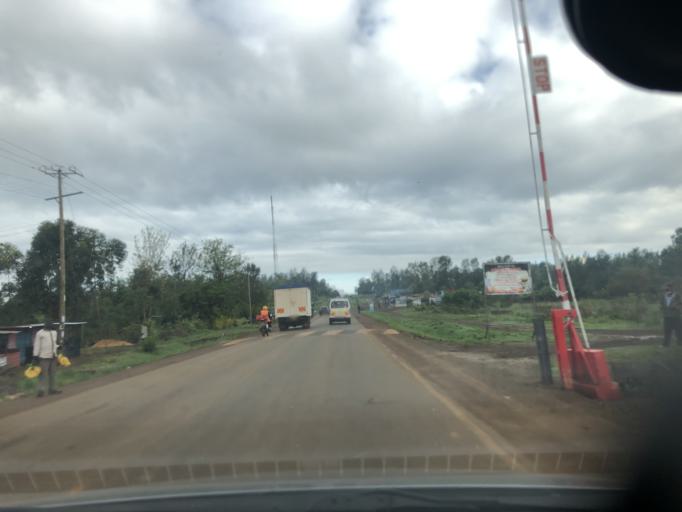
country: KE
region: Murang'a District
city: Maragua
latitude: -0.8385
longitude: 37.1381
